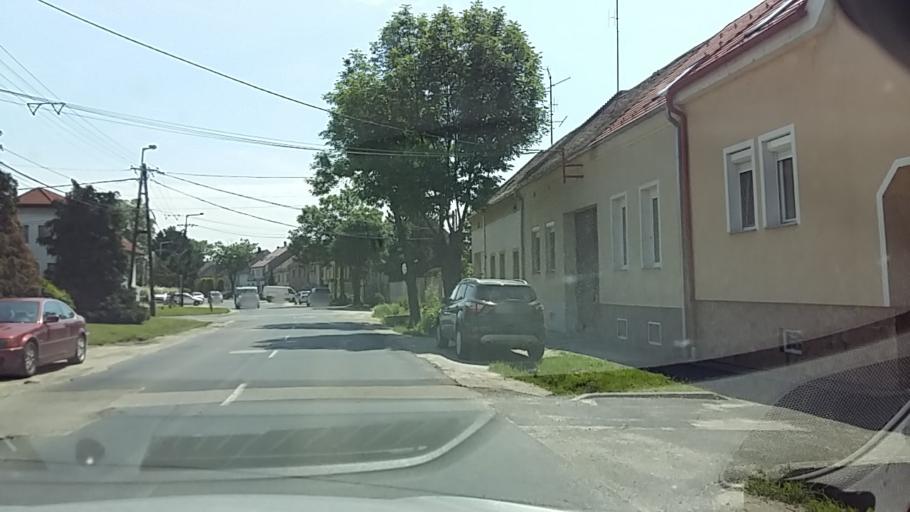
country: HU
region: Gyor-Moson-Sopron
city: Sopron
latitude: 47.6831
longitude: 16.6028
